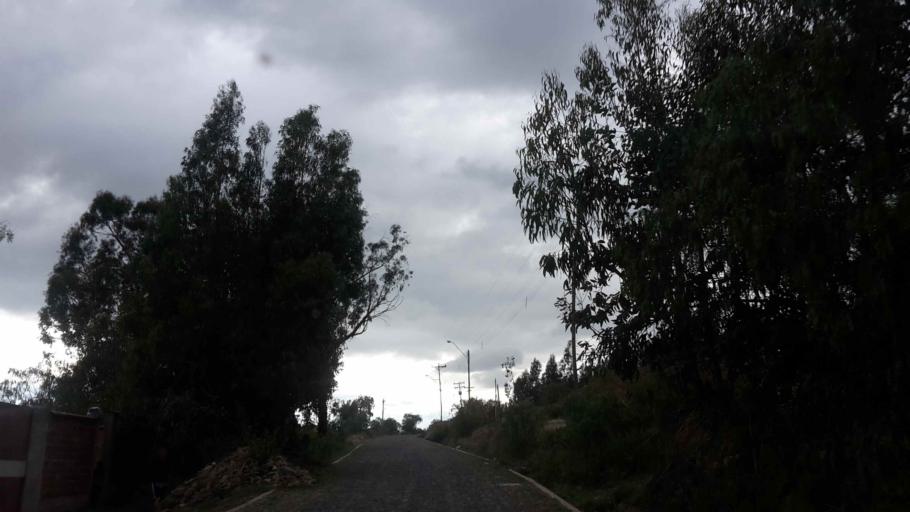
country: BO
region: Cochabamba
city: Cochabamba
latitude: -17.3735
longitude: -66.0575
